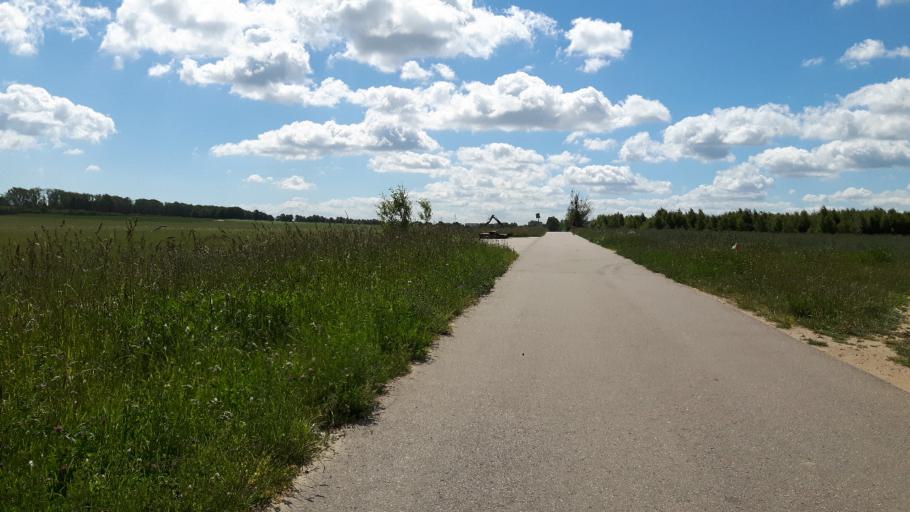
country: PL
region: Pomeranian Voivodeship
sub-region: Gdynia
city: Pogorze
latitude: 54.5725
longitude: 18.4991
